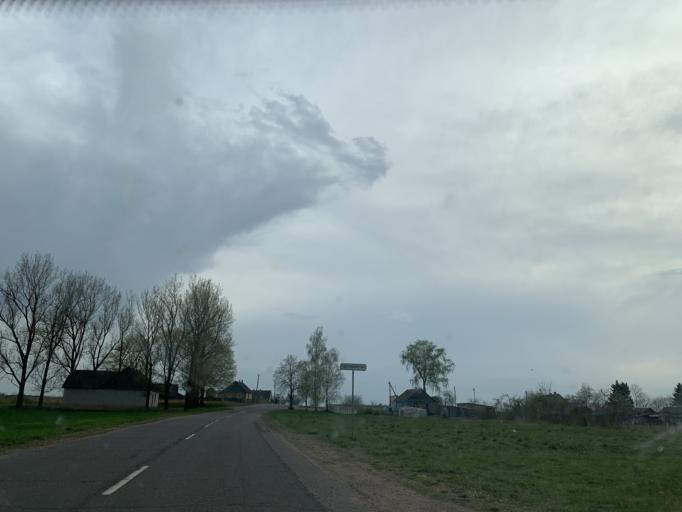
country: BY
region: Minsk
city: Kapyl'
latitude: 53.2952
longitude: 27.0352
